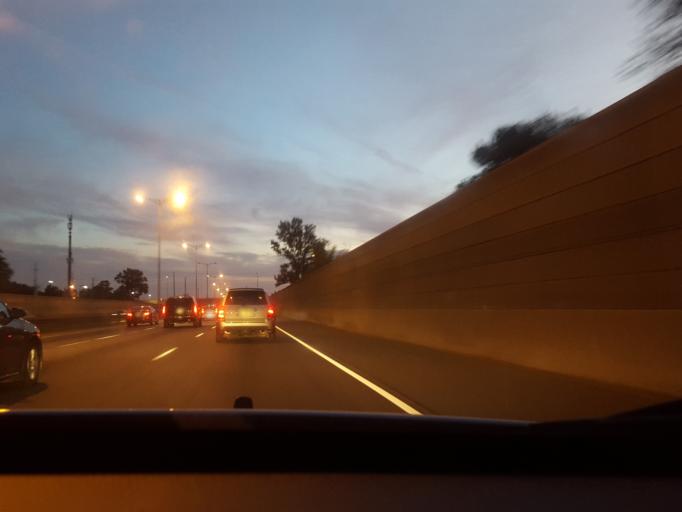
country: CA
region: Ontario
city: Etobicoke
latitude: 43.5988
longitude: -79.5667
